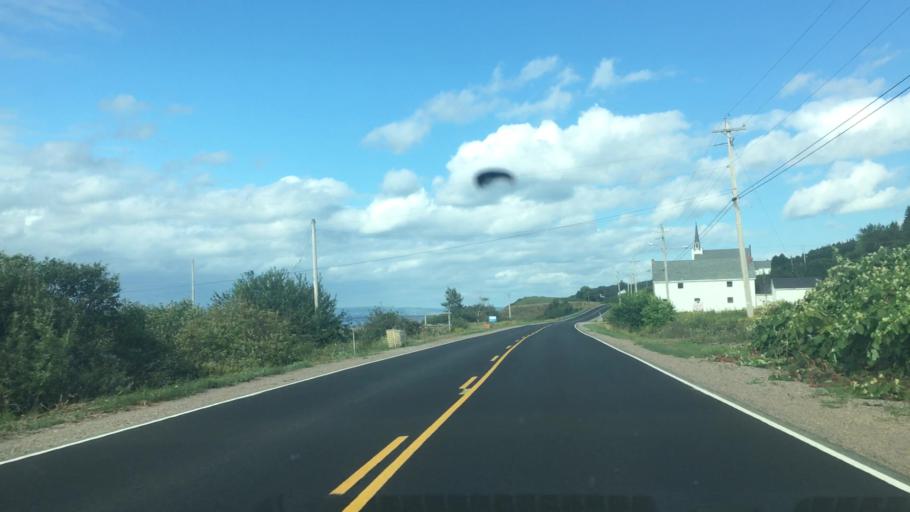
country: CA
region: Nova Scotia
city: Princeville
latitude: 45.7975
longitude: -60.7339
